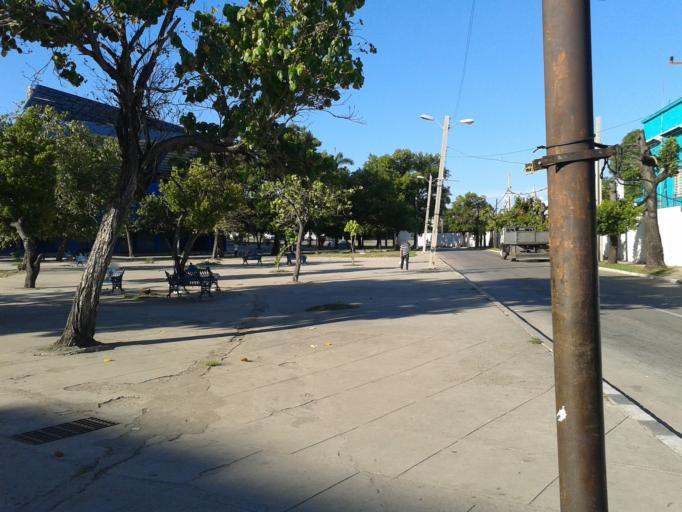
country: CU
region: La Habana
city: Cerro
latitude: 23.1199
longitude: -82.3767
